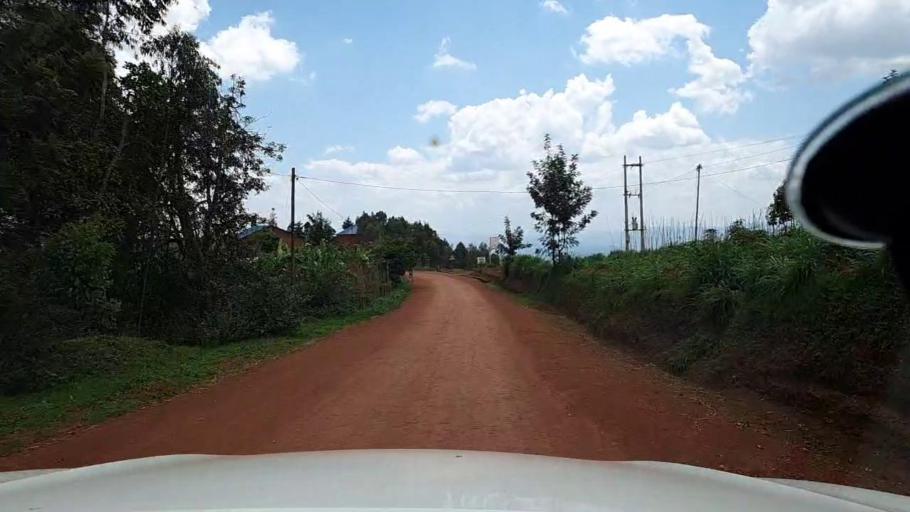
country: RW
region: Kigali
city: Kigali
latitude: -1.7970
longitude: 29.8445
